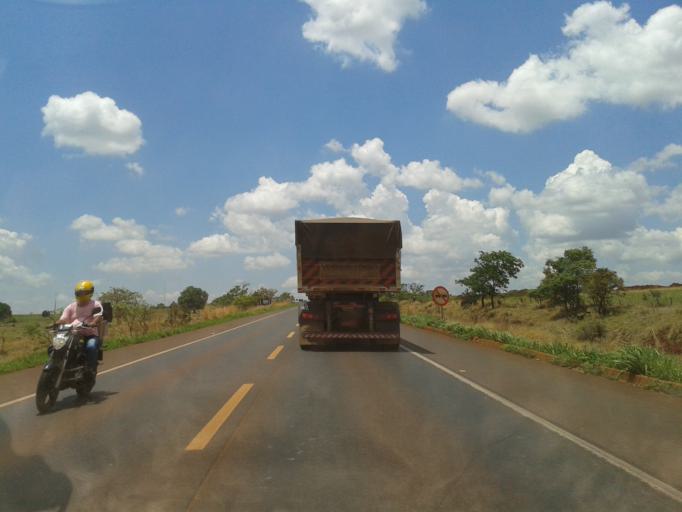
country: BR
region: Goias
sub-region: Itumbiara
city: Itumbiara
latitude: -18.3778
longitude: -49.3512
